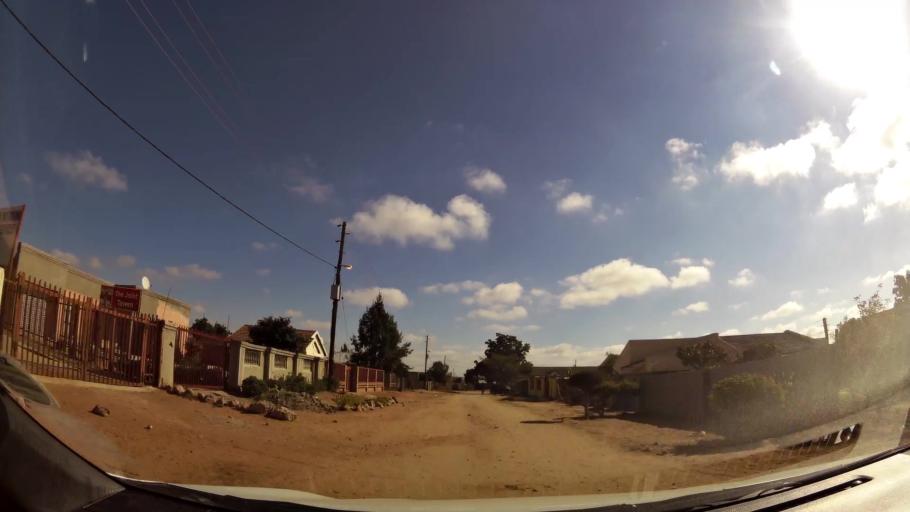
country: ZA
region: Limpopo
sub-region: Capricorn District Municipality
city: Polokwane
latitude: -23.8600
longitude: 29.3648
